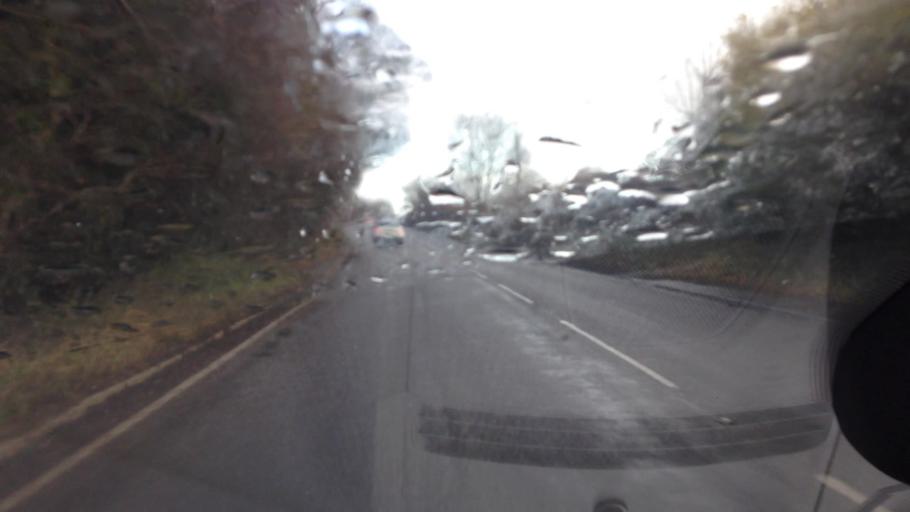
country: GB
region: England
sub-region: City and Borough of Leeds
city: Garforth
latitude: 53.7800
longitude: -1.3546
